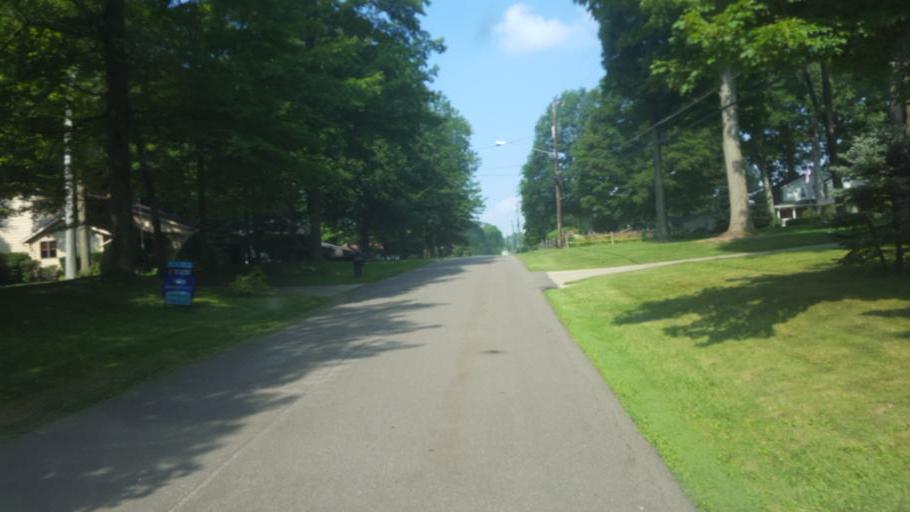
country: US
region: Ohio
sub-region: Richland County
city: Lexington
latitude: 40.6733
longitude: -82.5963
